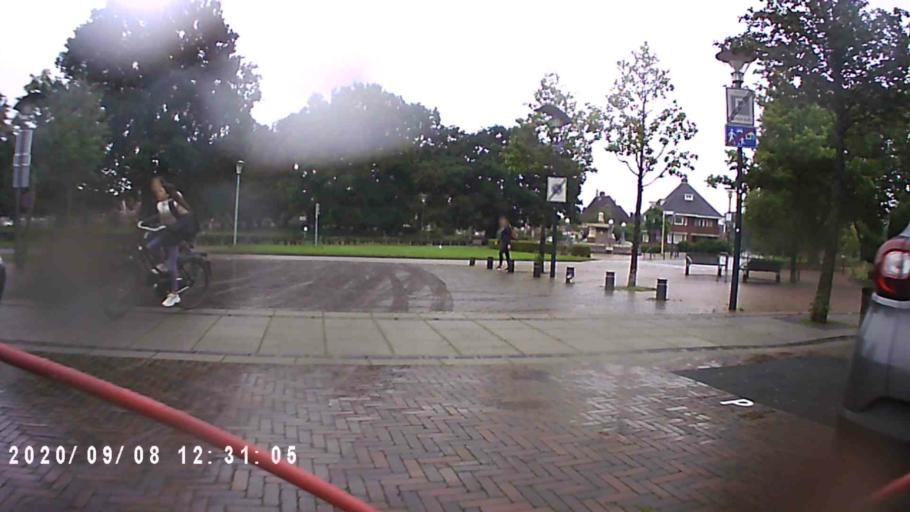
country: NL
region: Groningen
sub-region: Gemeente Veendam
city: Veendam
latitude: 53.1076
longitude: 6.8773
